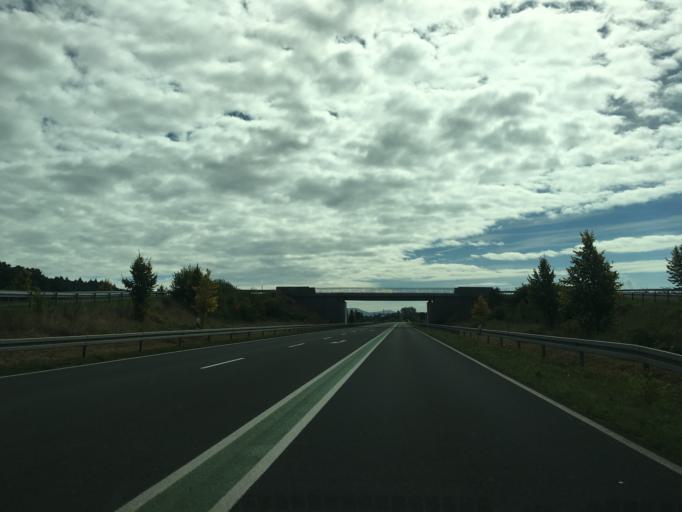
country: DE
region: Lower Saxony
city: Hameln
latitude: 52.1285
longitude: 9.3154
